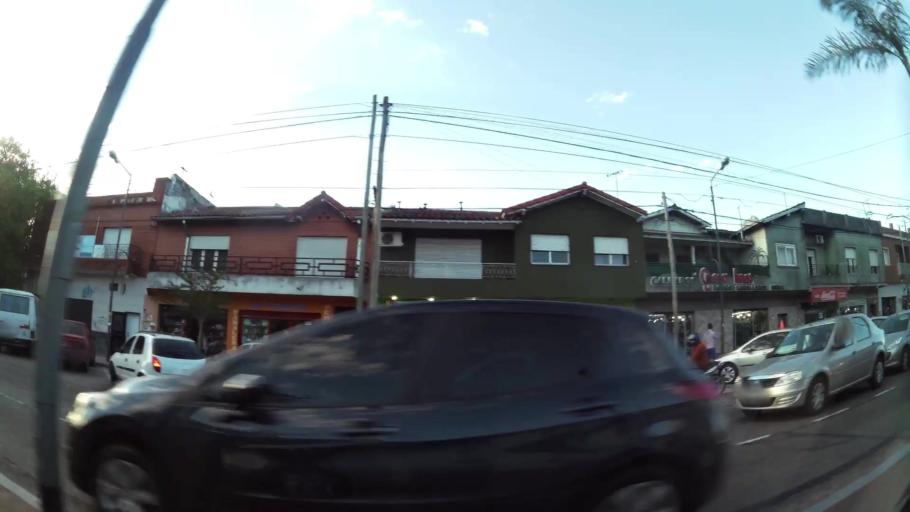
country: AR
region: Buenos Aires
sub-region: Partido de Tigre
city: Tigre
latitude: -34.4593
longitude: -58.5698
